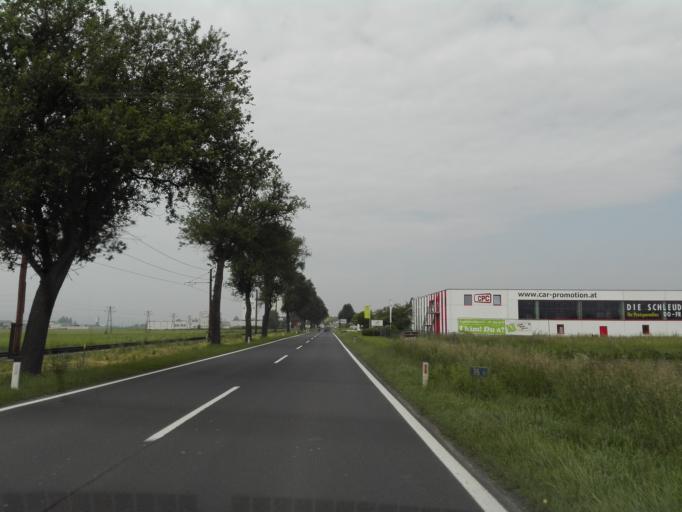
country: AT
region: Upper Austria
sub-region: Politischer Bezirk Urfahr-Umgebung
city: Goldworth
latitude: 48.2888
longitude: 14.1258
